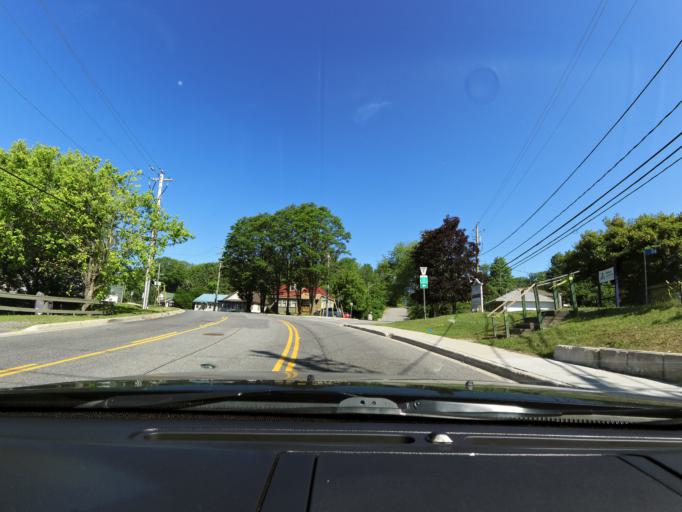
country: CA
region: Ontario
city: Huntsville
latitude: 45.3309
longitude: -79.2138
